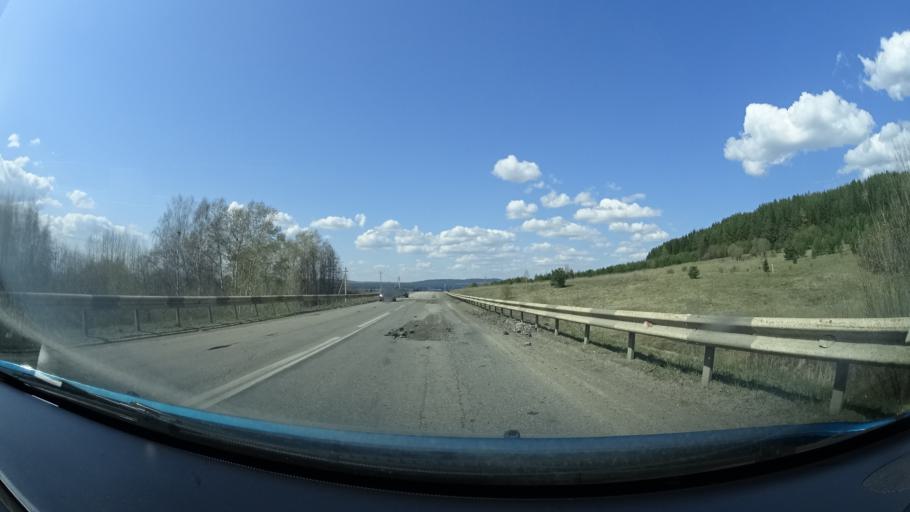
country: RU
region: Perm
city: Osa
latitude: 57.3275
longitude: 55.5954
